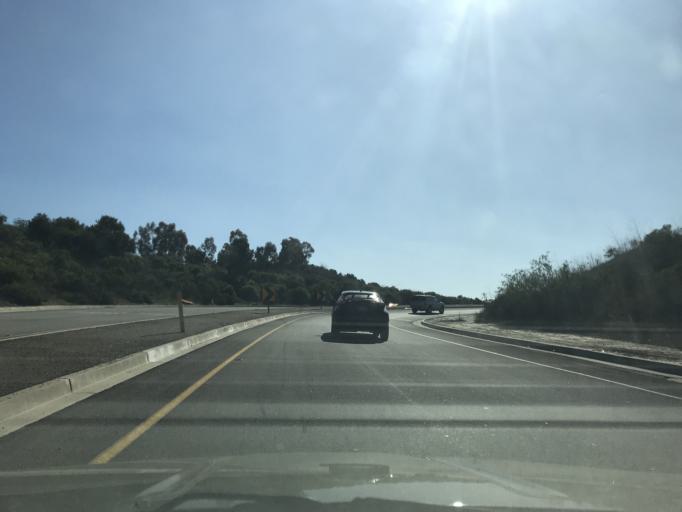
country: US
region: California
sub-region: Orange County
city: Irvine
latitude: 33.6490
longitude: -117.8587
